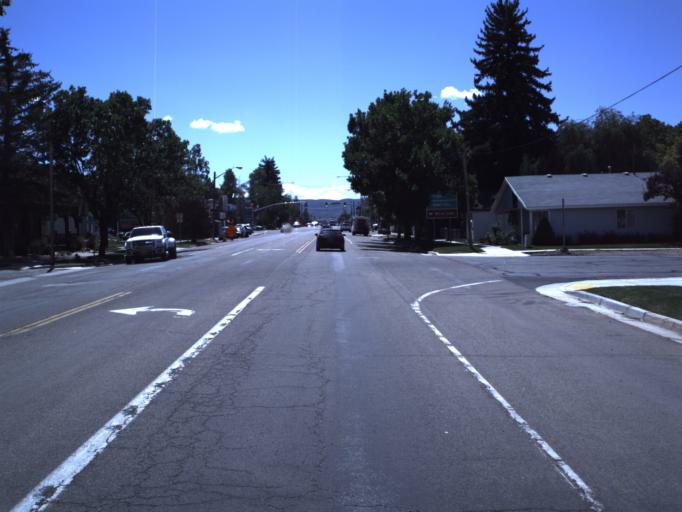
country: US
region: Utah
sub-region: Summit County
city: Kamas
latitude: 40.6451
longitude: -111.2808
